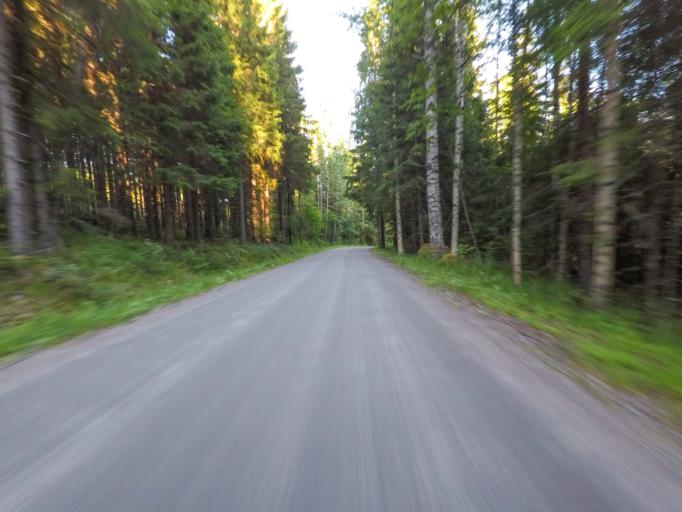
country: FI
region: Northern Savo
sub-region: Kuopio
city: Maaninka
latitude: 62.8823
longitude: 27.2930
